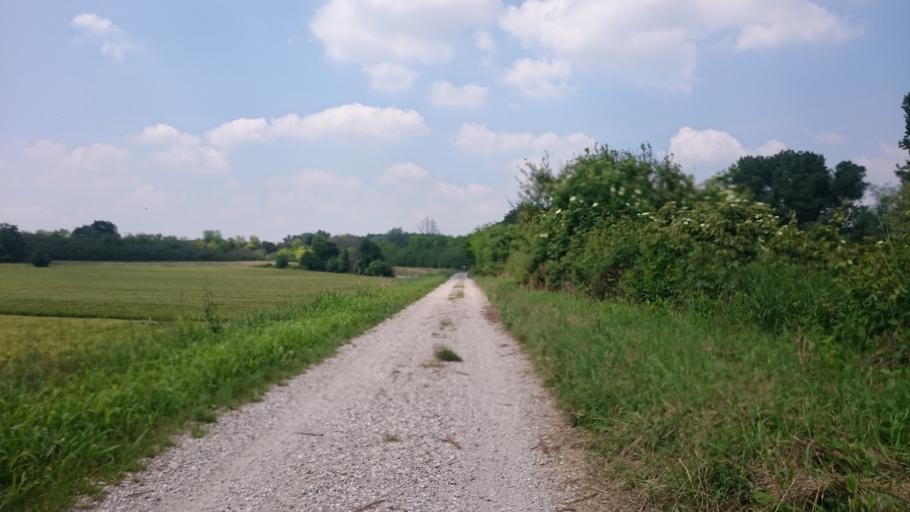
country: IT
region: Lombardy
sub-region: Provincia di Mantova
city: Lunetta-Frassino
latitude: 45.1296
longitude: 10.8193
